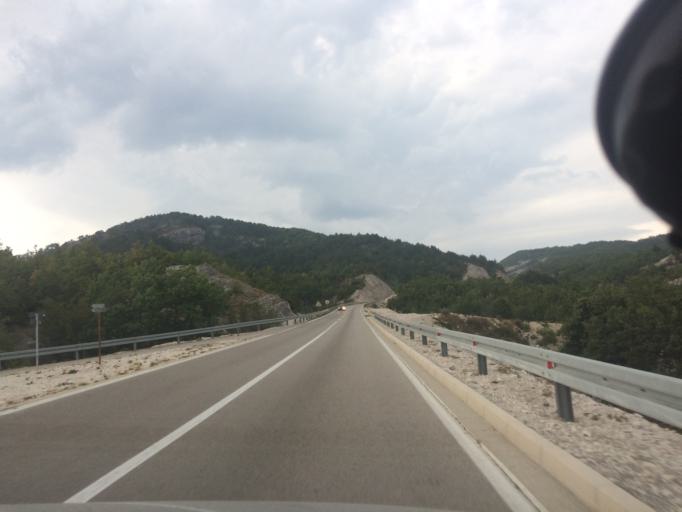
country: ME
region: Kotor
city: Risan
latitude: 42.6702
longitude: 18.6499
